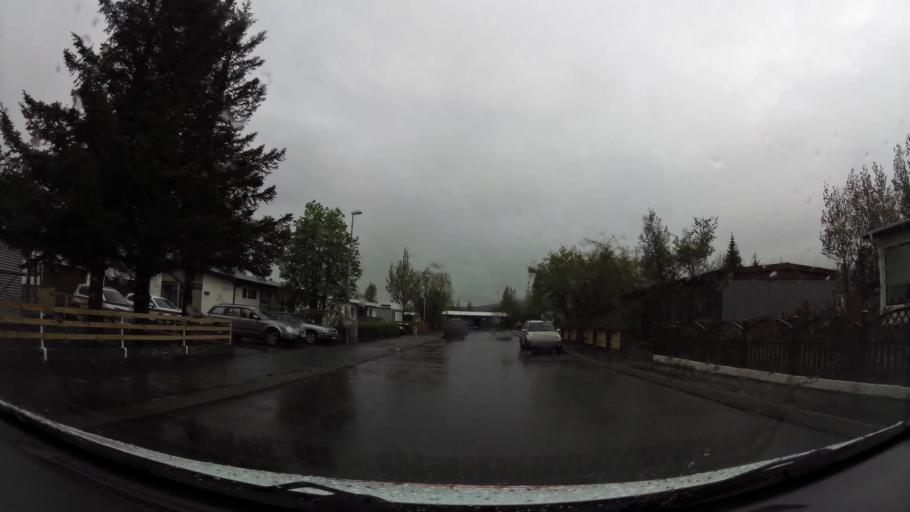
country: IS
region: South
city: Hveragerdi
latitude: 64.0030
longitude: -21.1966
